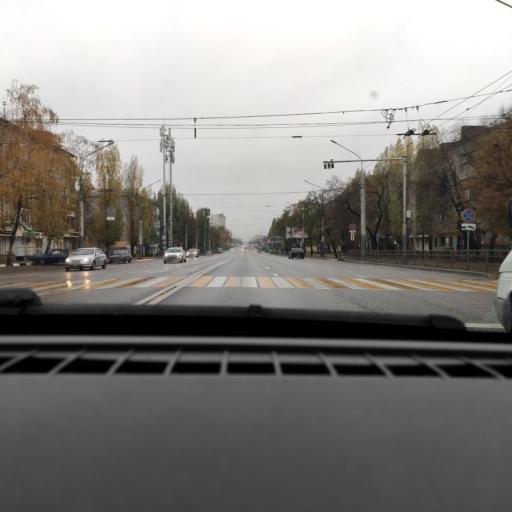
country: RU
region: Voronezj
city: Voronezh
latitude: 51.6698
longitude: 39.2513
